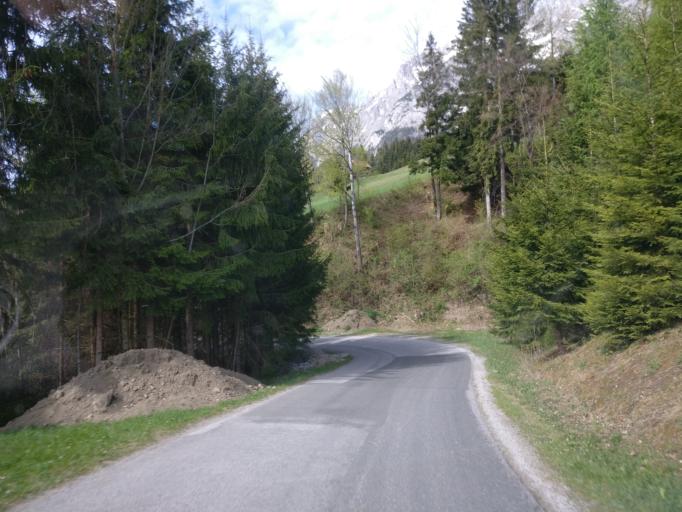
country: AT
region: Salzburg
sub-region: Politischer Bezirk Sankt Johann im Pongau
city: Pfarrwerfen
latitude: 47.4724
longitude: 13.2043
